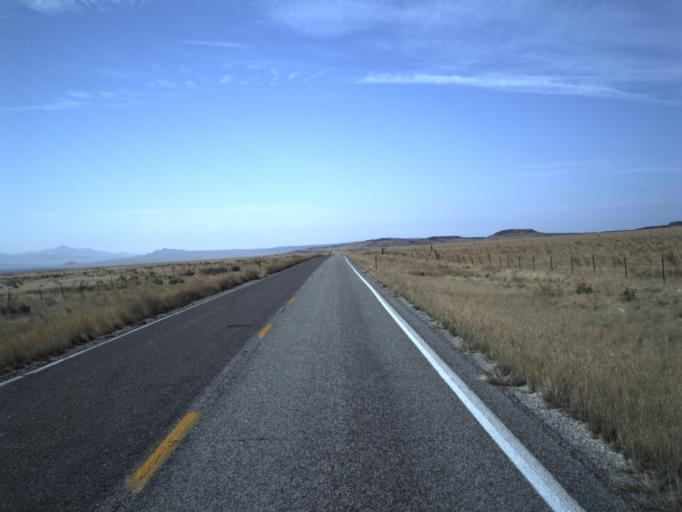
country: US
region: Idaho
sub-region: Oneida County
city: Malad City
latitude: 41.8720
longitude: -113.1224
